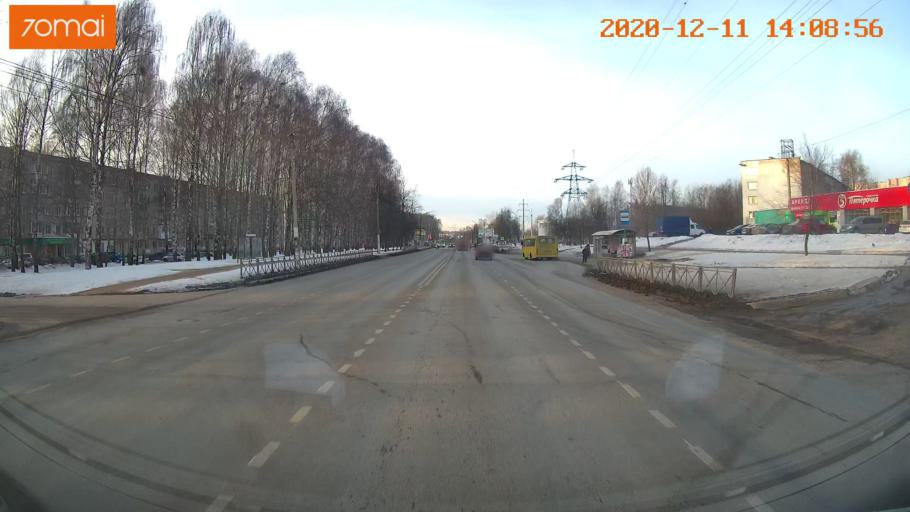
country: RU
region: Kostroma
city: Oktyabr'skiy
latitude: 57.7379
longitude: 40.9910
